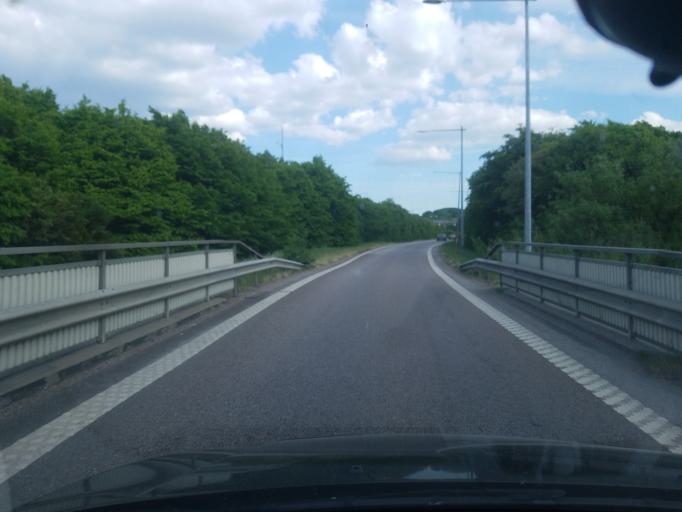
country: SE
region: Vaestra Goetaland
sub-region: Goteborg
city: Majorna
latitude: 57.6457
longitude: 11.9282
